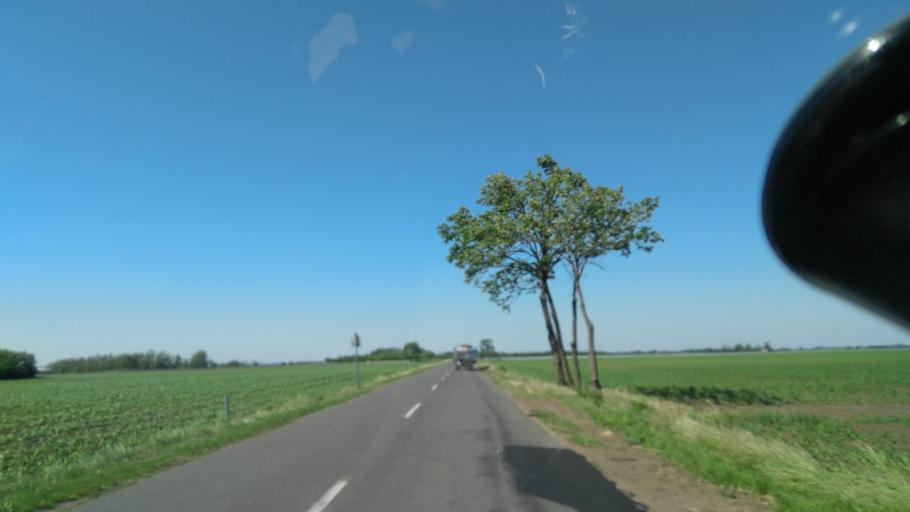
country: HU
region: Bekes
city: Kevermes
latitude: 46.4344
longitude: 21.1725
